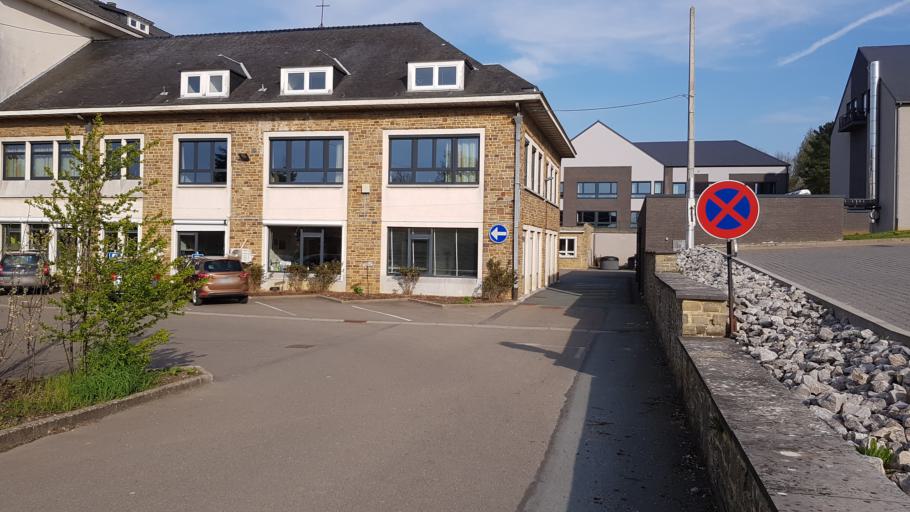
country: BE
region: Wallonia
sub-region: Province de Namur
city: Dinant
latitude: 50.2631
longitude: 4.9236
